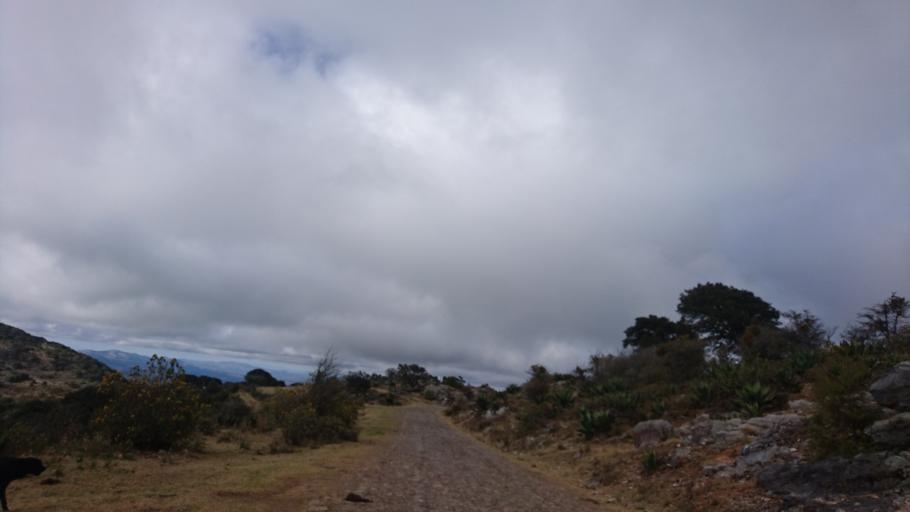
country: MX
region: San Luis Potosi
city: Zaragoza
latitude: 22.0747
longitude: -100.6412
